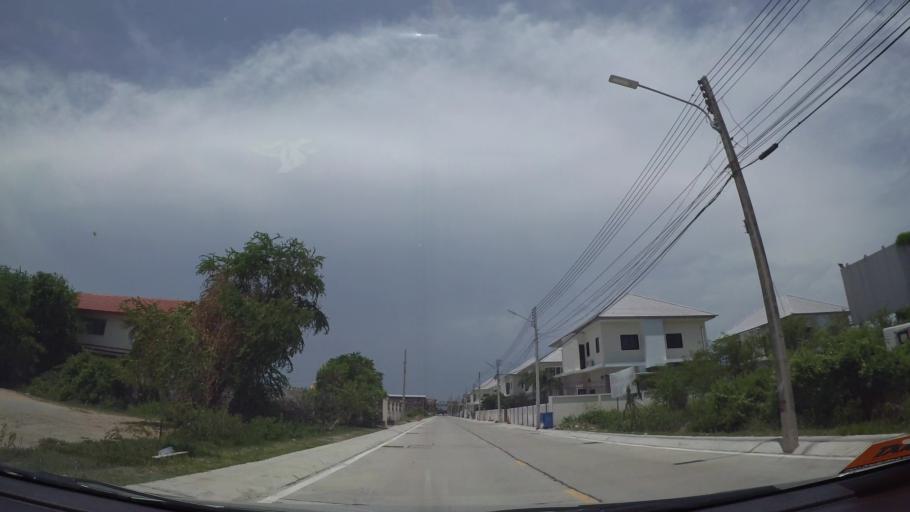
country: TH
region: Chon Buri
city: Chon Buri
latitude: 13.3405
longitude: 100.9467
